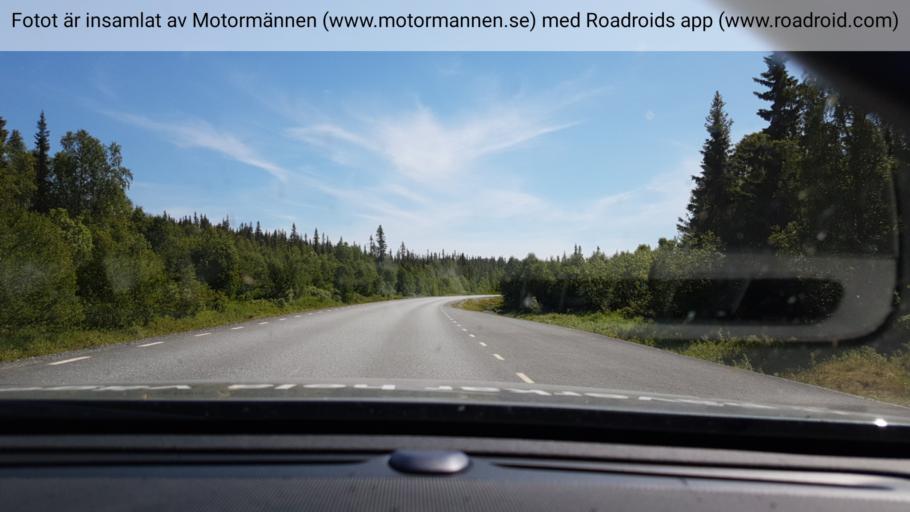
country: SE
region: Vaesterbotten
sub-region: Vilhelmina Kommun
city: Sjoberg
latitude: 64.8106
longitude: 15.2626
